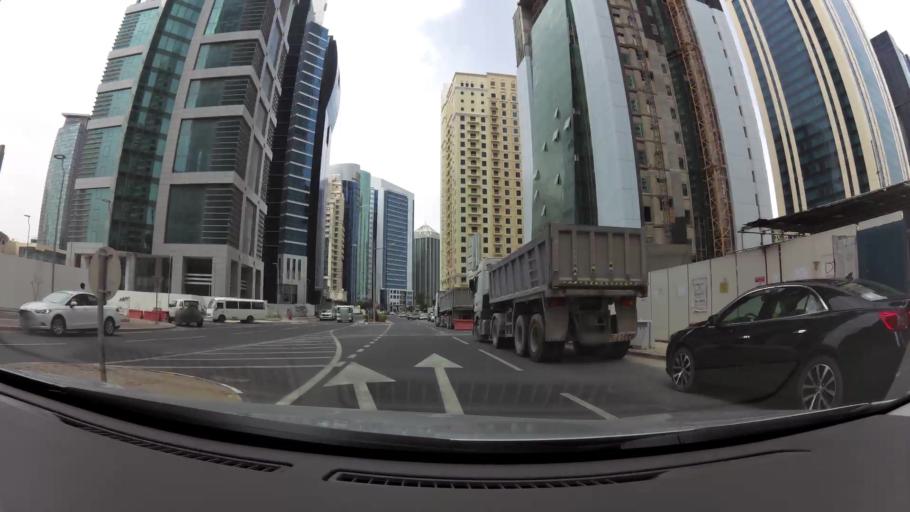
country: QA
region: Baladiyat ad Dawhah
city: Doha
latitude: 25.3272
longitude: 51.5317
